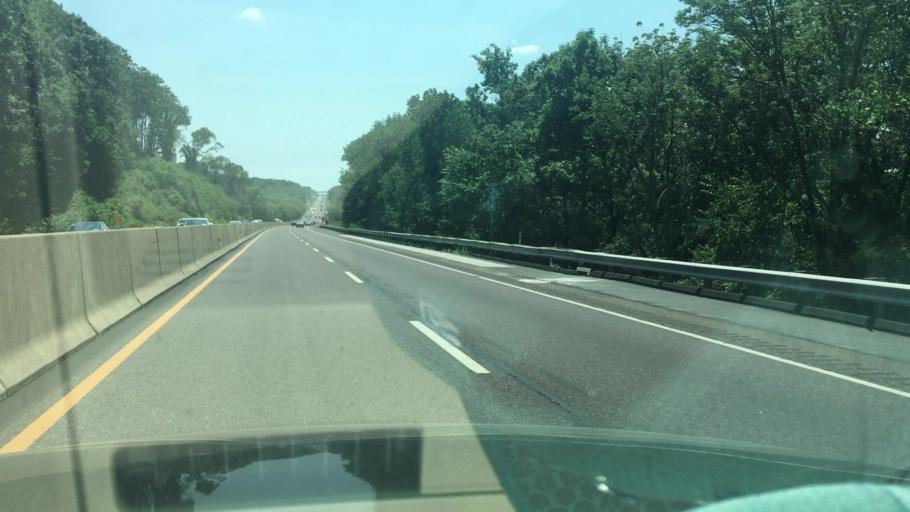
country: US
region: Pennsylvania
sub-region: Bucks County
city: Spinnerstown
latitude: 40.3758
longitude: -75.4047
